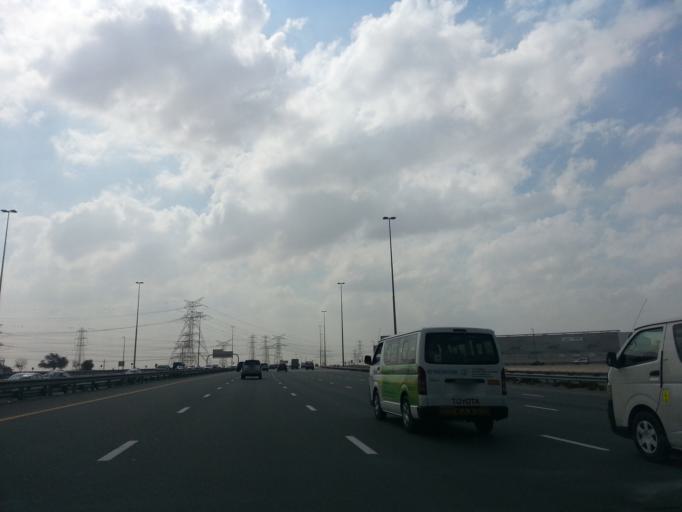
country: AE
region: Dubai
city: Dubai
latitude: 25.1438
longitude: 55.2610
